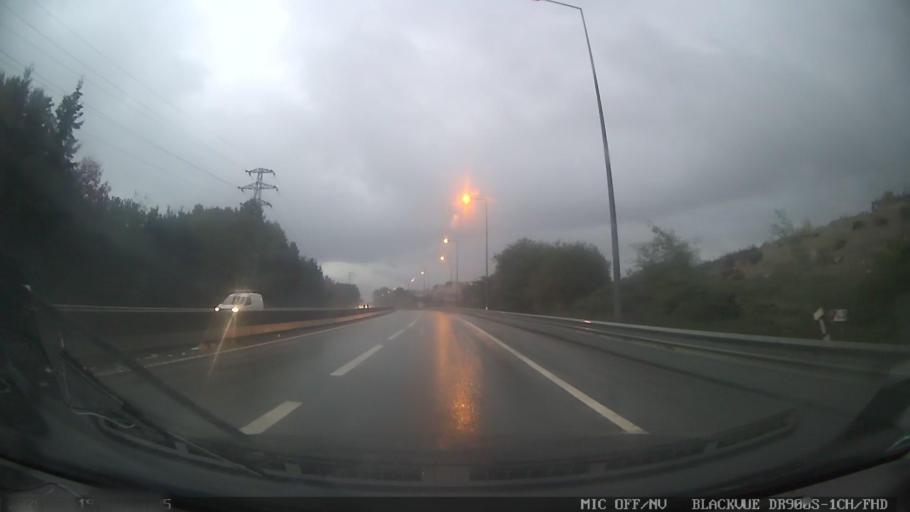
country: PT
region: Vila Real
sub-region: Vila Real
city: Vila Real
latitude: 41.3129
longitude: -7.7451
